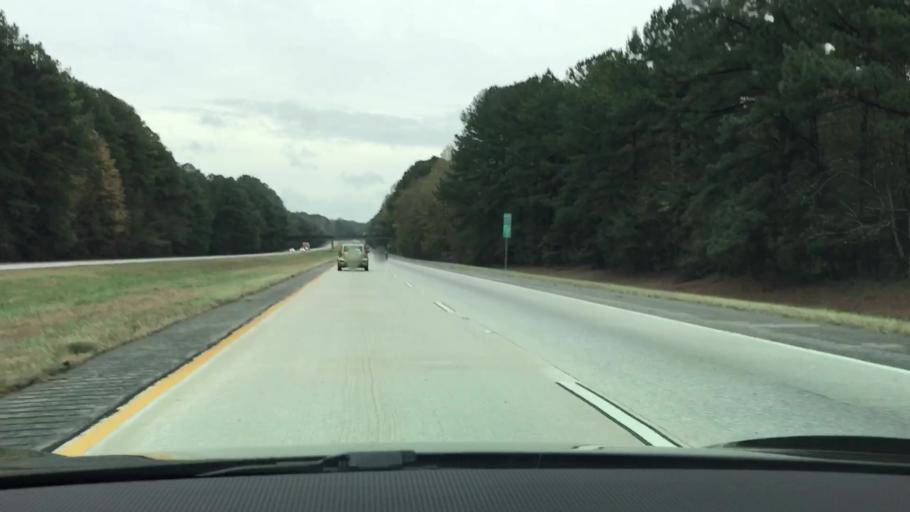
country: US
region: Georgia
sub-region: Greene County
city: Union Point
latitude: 33.5490
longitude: -83.0485
